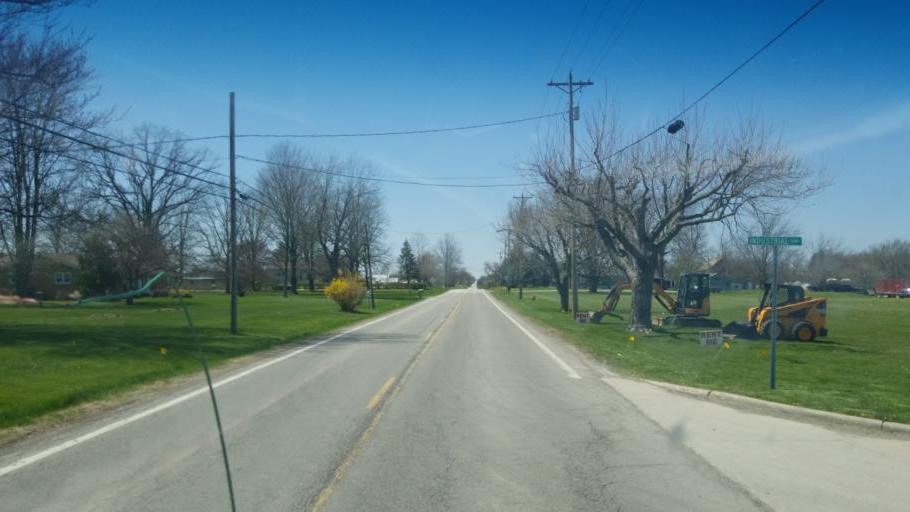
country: US
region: Ohio
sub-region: Huron County
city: New London
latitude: 41.0861
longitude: -82.4113
